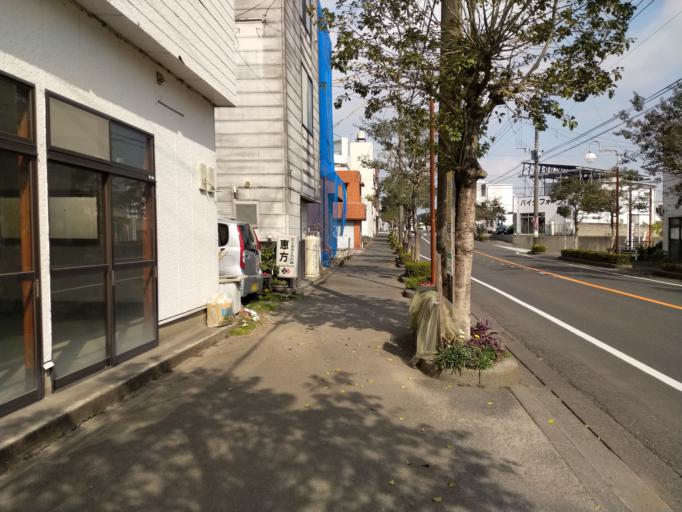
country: JP
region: Kagoshima
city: Kanoya
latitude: 31.3913
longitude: 130.8518
